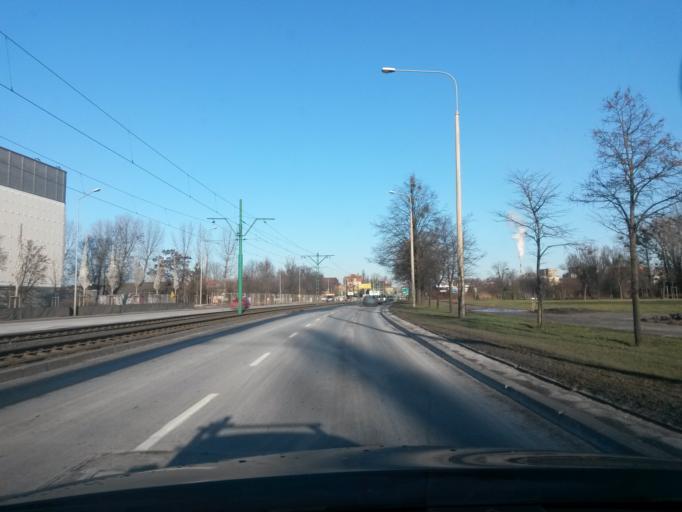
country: PL
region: Greater Poland Voivodeship
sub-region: Poznan
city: Poznan
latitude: 52.4066
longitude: 16.9542
